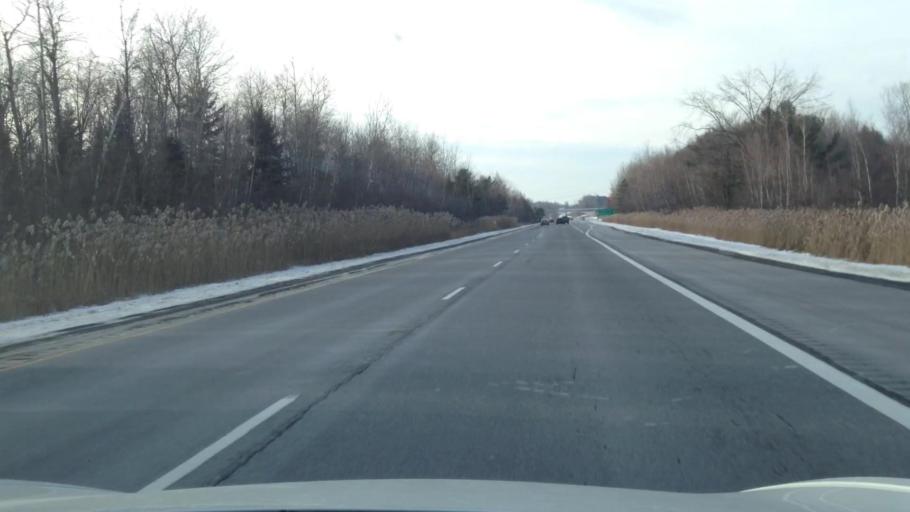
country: CA
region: Quebec
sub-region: Laurentides
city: Brownsburg-Chatham
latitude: 45.5512
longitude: -74.4391
